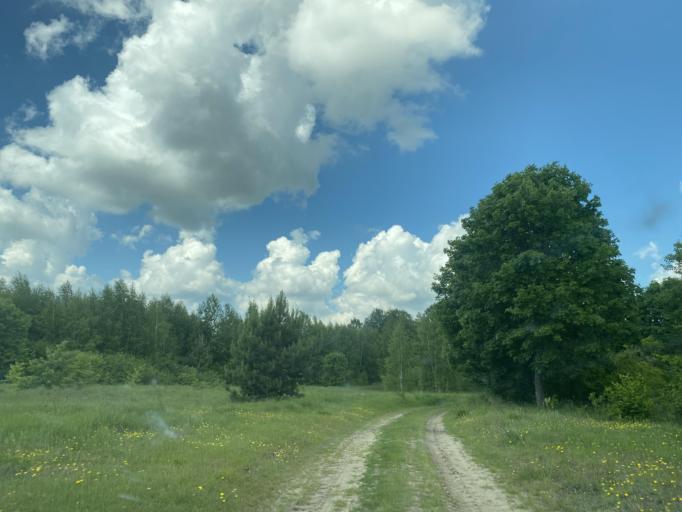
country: BY
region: Brest
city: Ivanava
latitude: 52.2025
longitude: 25.6096
